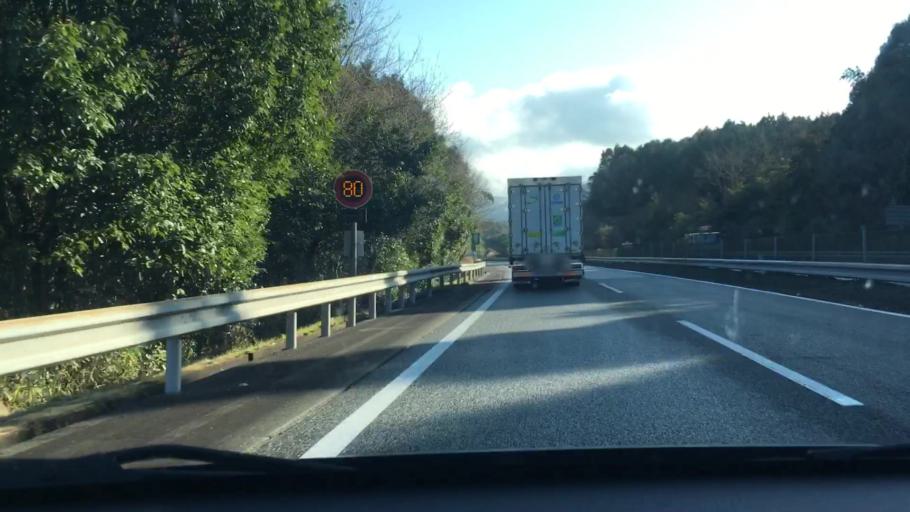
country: JP
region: Kumamoto
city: Hitoyoshi
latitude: 32.1667
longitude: 130.7930
